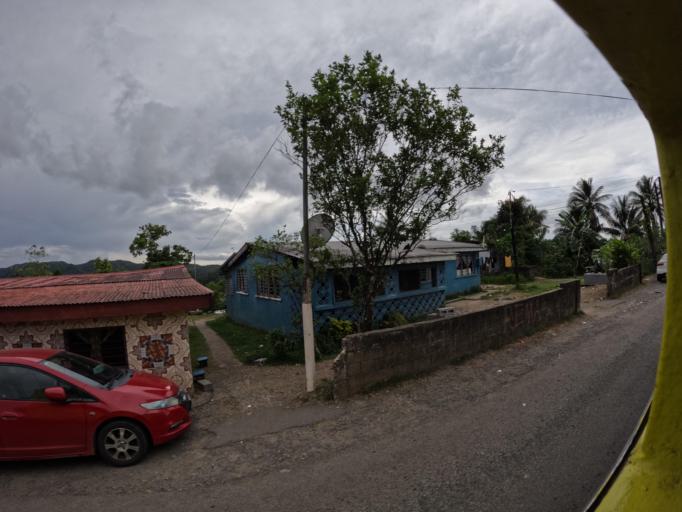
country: FJ
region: Central
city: Suva
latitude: -18.0807
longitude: 178.4569
